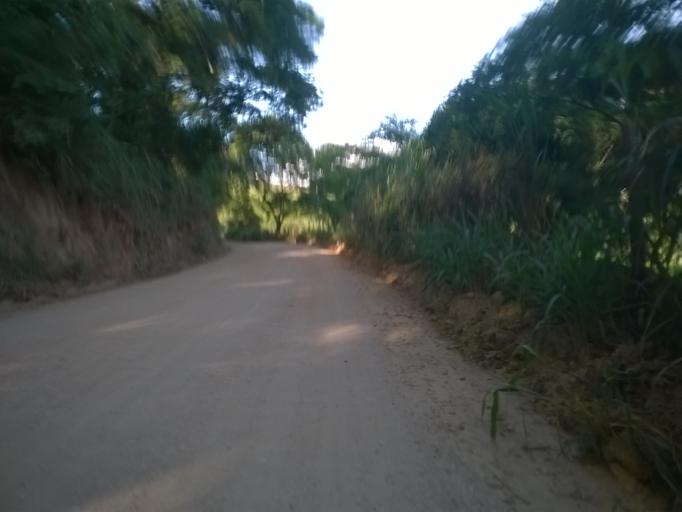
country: BR
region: Minas Gerais
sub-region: Uba
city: Uba
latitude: -21.0837
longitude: -43.0002
